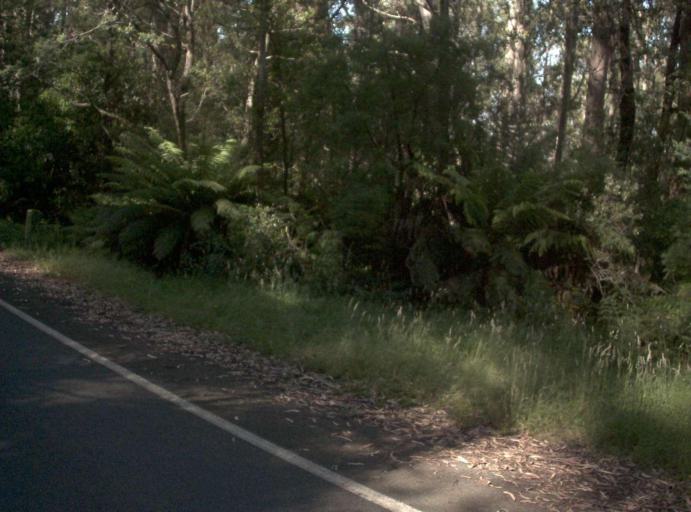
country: AU
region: Victoria
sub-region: Yarra Ranges
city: Millgrove
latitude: -37.7167
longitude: 145.6905
